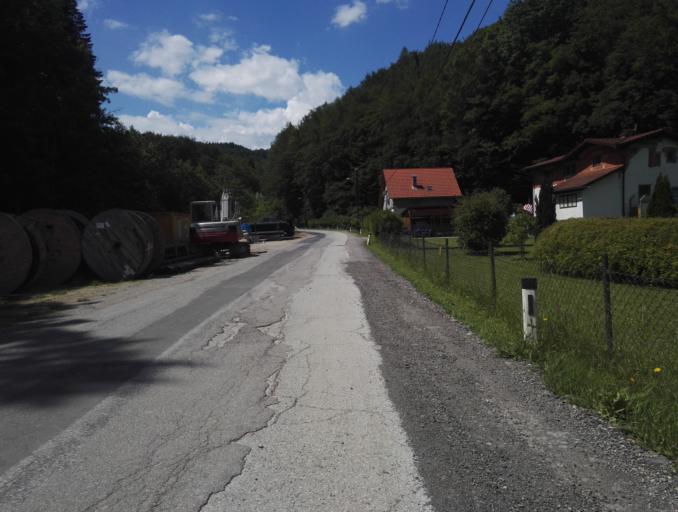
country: AT
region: Styria
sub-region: Politischer Bezirk Graz-Umgebung
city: Gratwein
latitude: 47.1049
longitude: 15.3168
